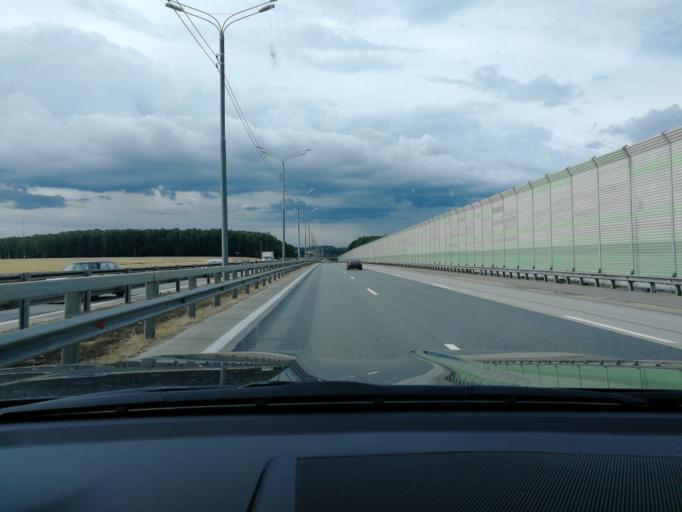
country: RU
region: Moskovskaya
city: Barybino
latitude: 55.2635
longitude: 37.8673
